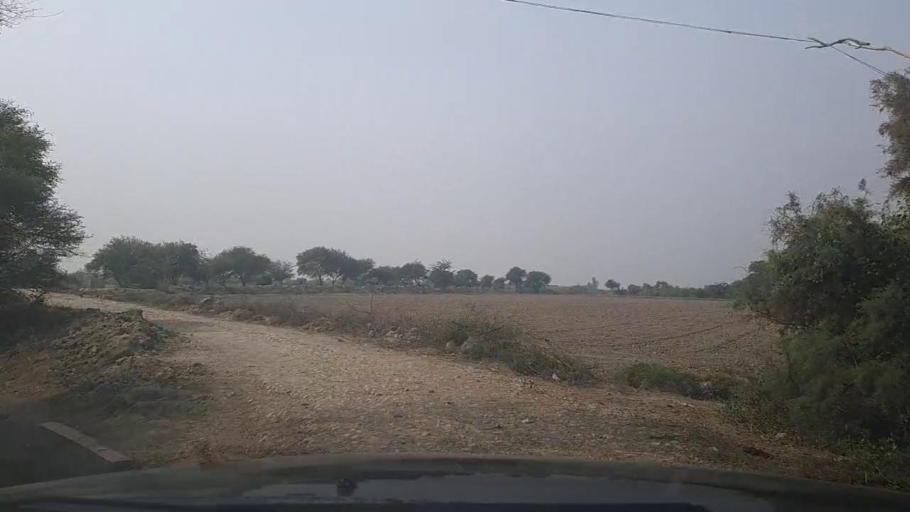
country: PK
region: Sindh
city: Mirpur Sakro
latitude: 24.5297
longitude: 67.7955
